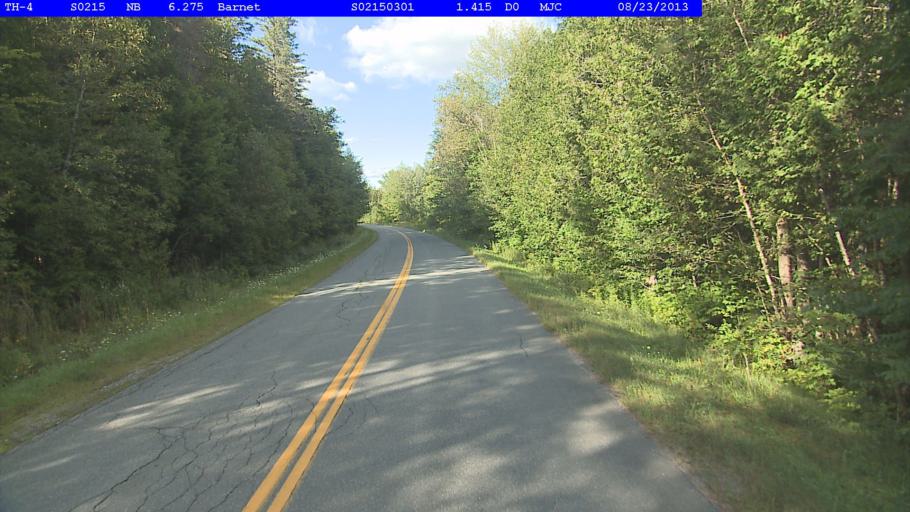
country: US
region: New Hampshire
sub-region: Grafton County
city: Woodsville
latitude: 44.2925
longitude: -72.1634
